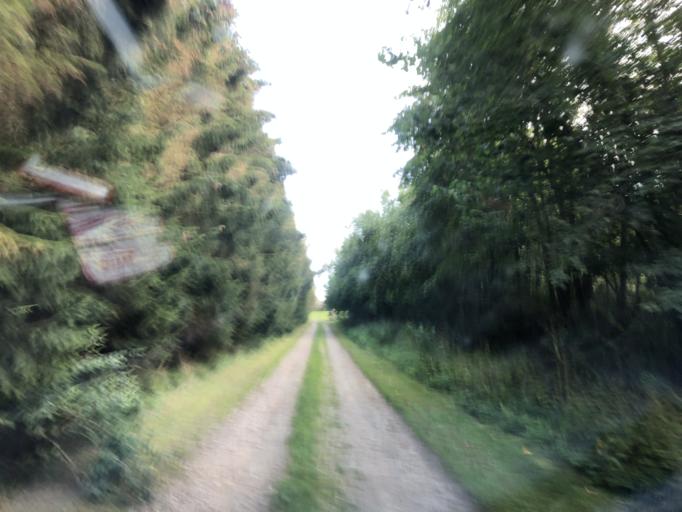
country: DK
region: Central Jutland
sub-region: Favrskov Kommune
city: Hadsten
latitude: 56.3210
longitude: 10.0230
